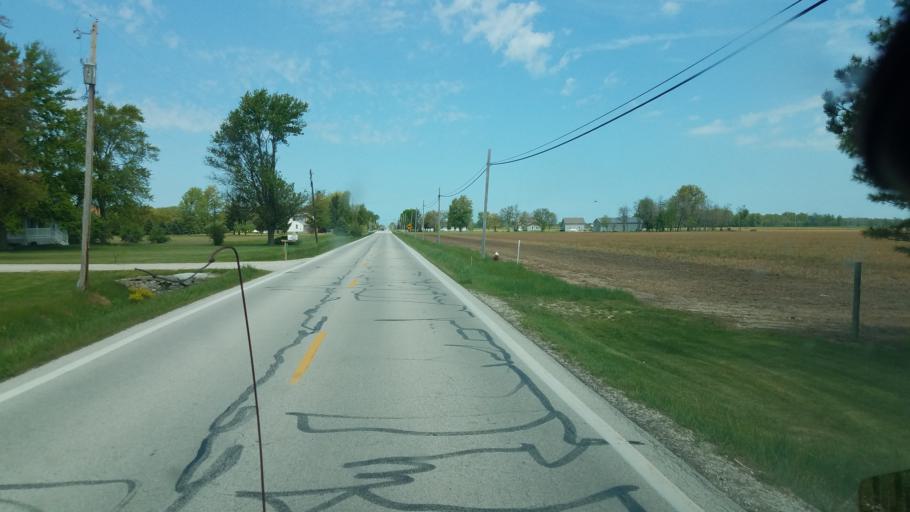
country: US
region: Ohio
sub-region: Ottawa County
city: Oak Harbor
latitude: 41.5631
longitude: -83.1448
